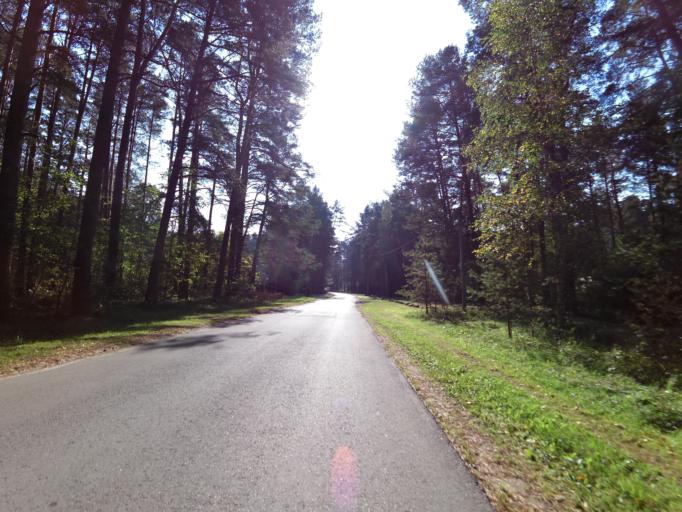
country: LT
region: Vilnius County
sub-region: Vilnius
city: Vilnius
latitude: 54.7374
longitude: 25.3066
